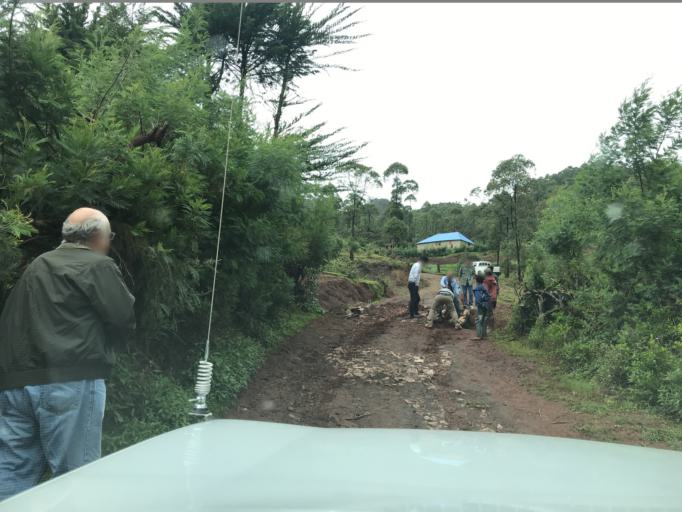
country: TL
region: Ainaro
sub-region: Ainaro
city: Ainaro
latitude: -8.8741
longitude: 125.5511
